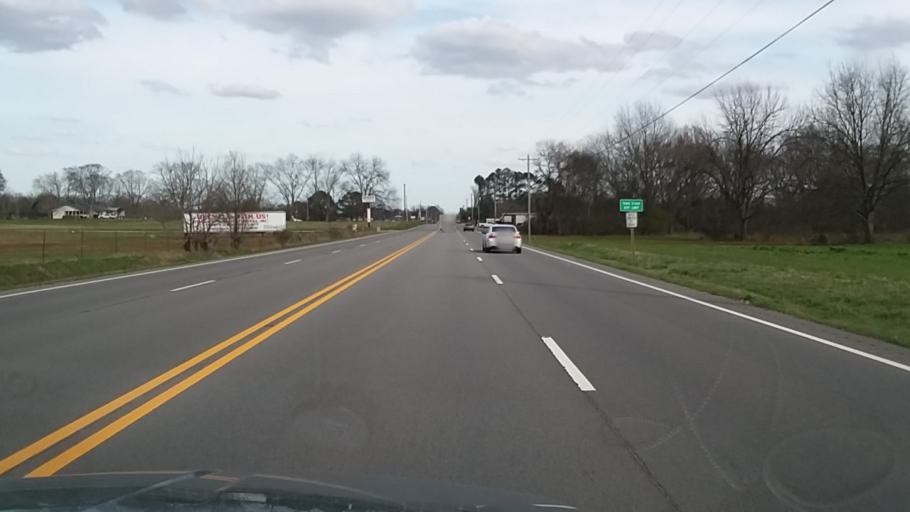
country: US
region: Alabama
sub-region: Lawrence County
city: Town Creek
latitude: 34.6815
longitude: -87.4233
